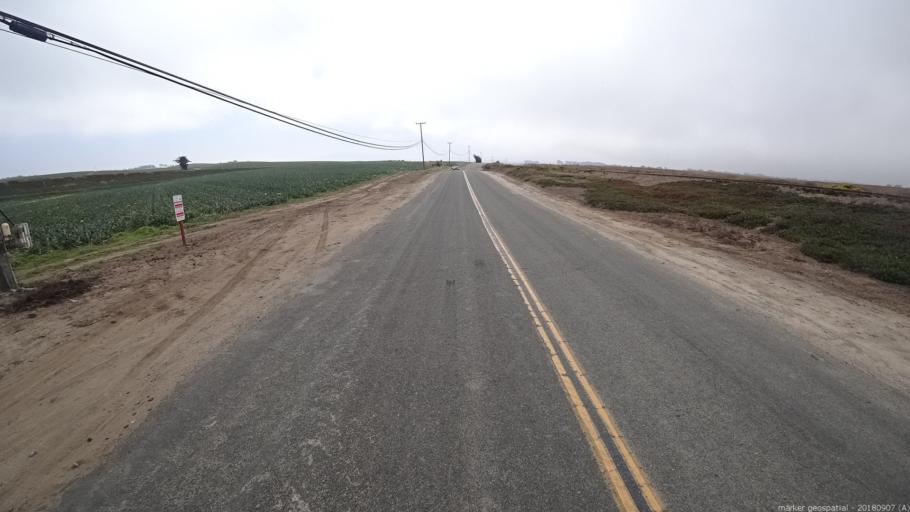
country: US
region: California
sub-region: Monterey County
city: Marina
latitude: 36.7113
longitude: -121.7906
